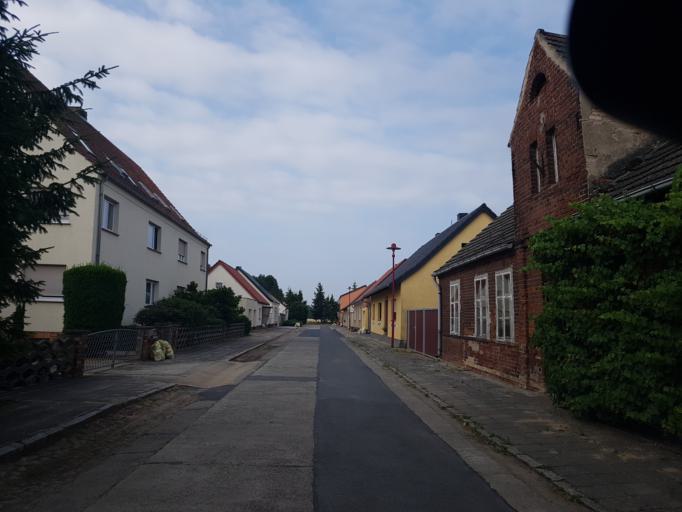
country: DE
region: Saxony-Anhalt
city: Seyda
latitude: 51.9538
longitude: 12.8947
